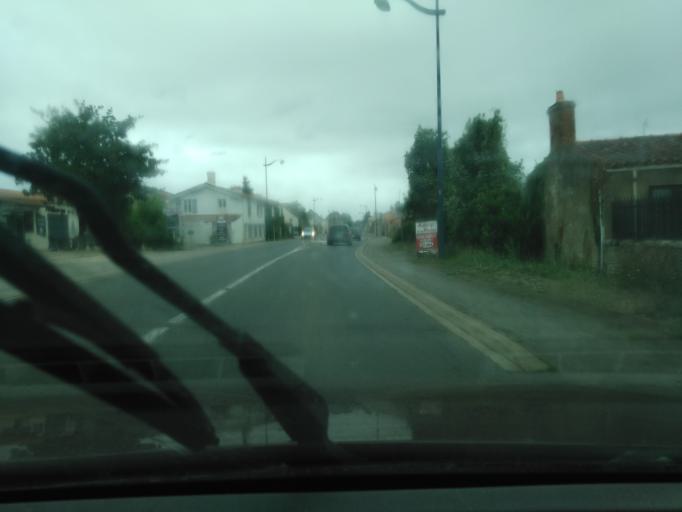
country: FR
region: Pays de la Loire
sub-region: Departement de la Vendee
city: Sainte-Gemme-la-Plaine
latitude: 46.4787
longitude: -1.1120
